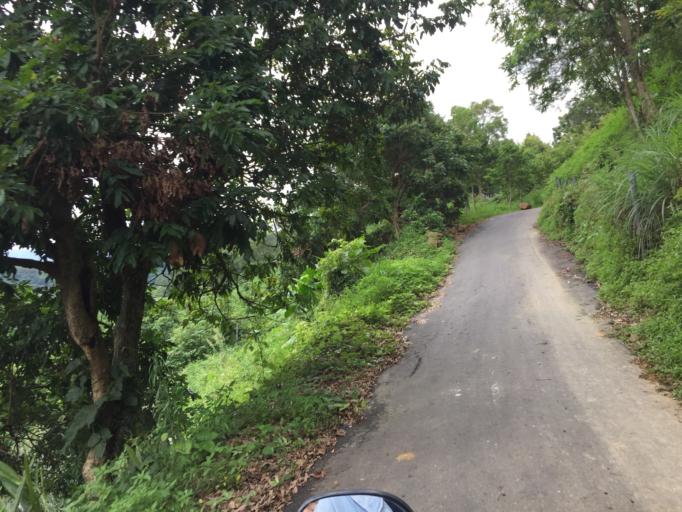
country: TW
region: Taiwan
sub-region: Taichung City
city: Taichung
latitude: 24.0646
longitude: 120.7166
